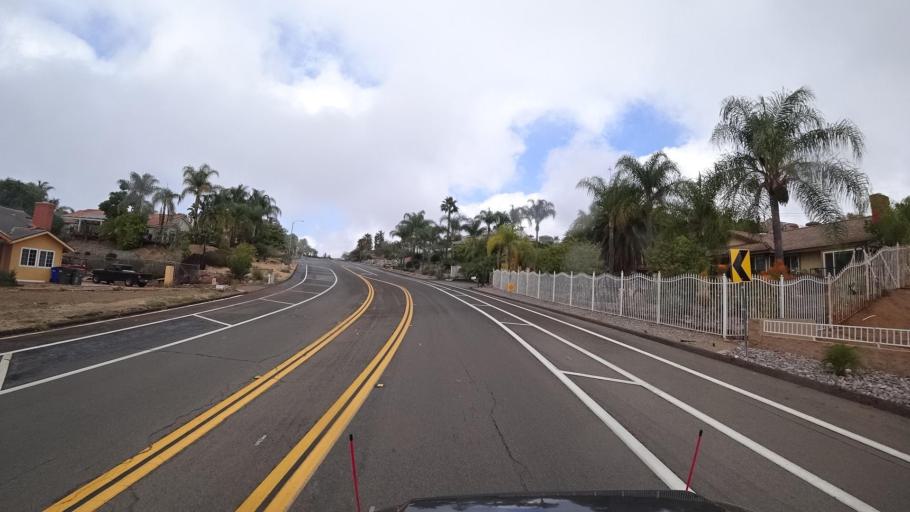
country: US
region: California
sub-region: San Diego County
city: Granite Hills
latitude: 32.7728
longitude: -116.9069
